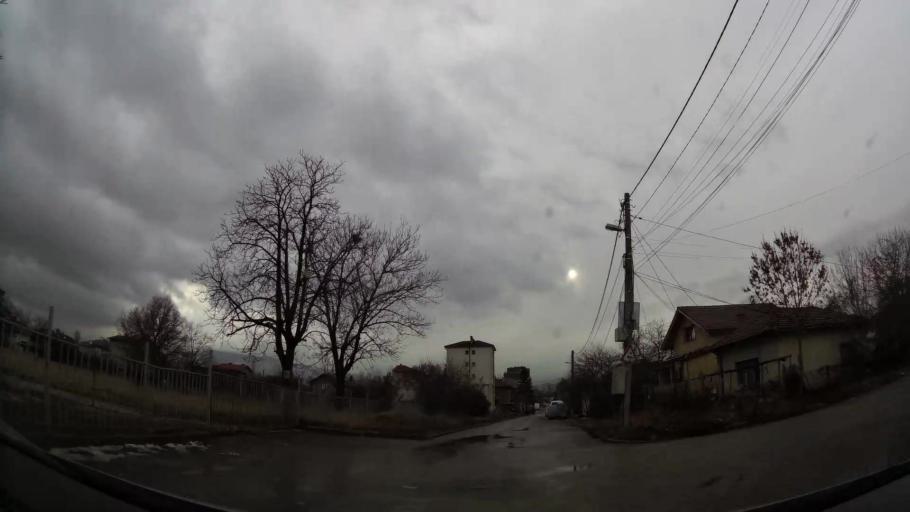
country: BG
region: Sofia-Capital
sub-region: Stolichna Obshtina
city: Sofia
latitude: 42.7261
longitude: 23.2697
